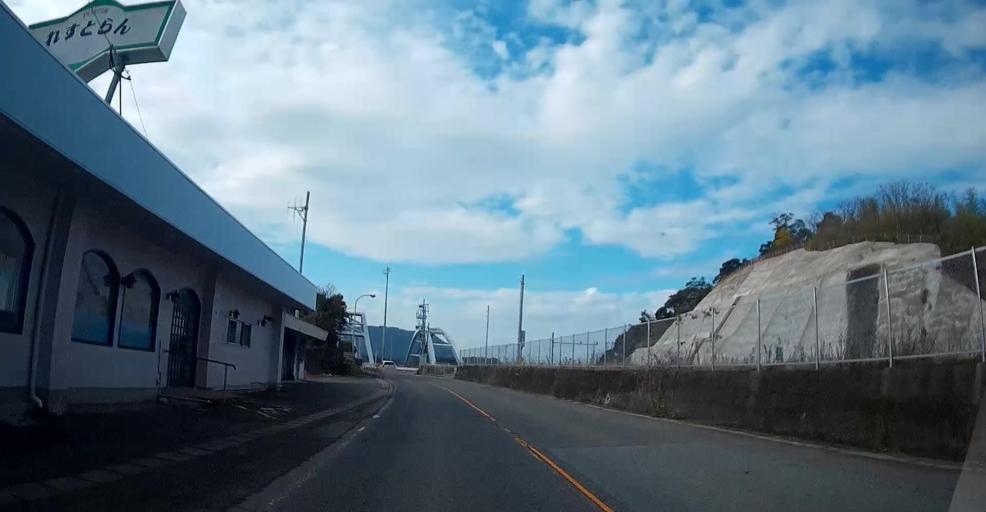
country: JP
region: Kumamoto
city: Yatsushiro
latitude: 32.6100
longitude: 130.4619
